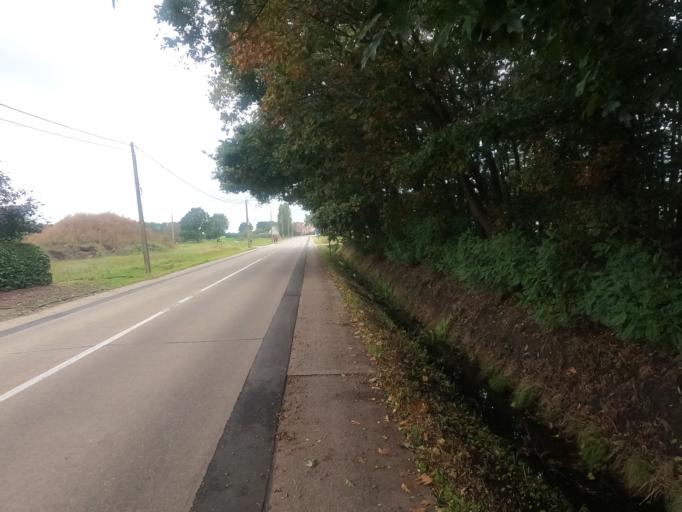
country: BE
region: Flanders
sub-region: Provincie Antwerpen
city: Berlaar
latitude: 51.1279
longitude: 4.6957
